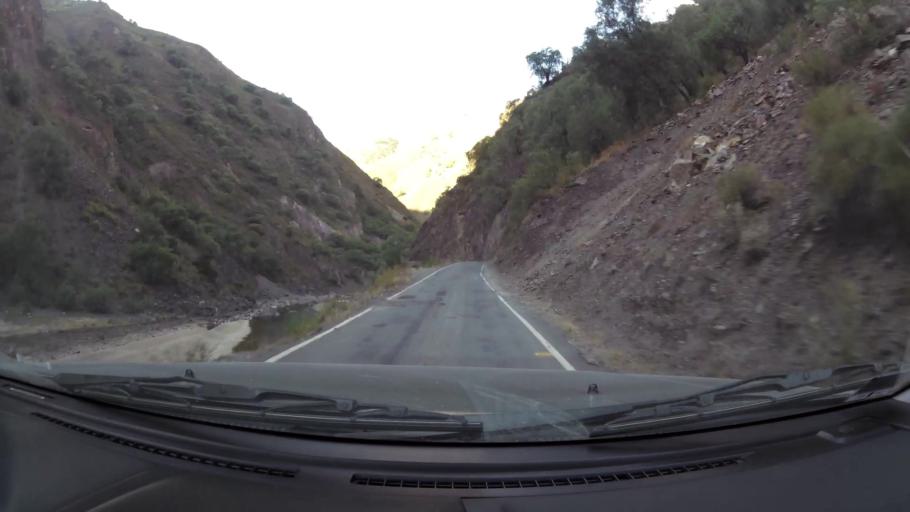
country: PE
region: Huancavelica
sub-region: Provincia de Churcampa
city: La Esmeralda
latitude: -12.5499
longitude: -74.7047
